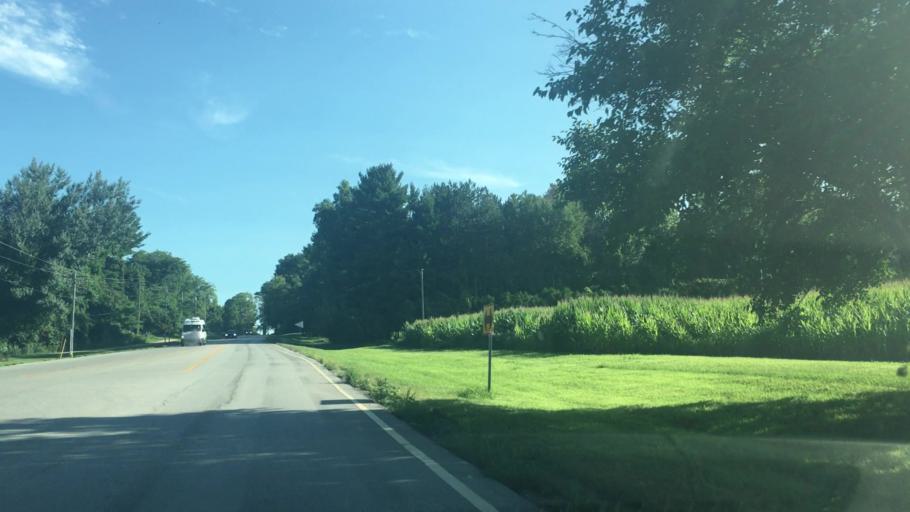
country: US
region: Iowa
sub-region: Johnson County
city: Iowa City
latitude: 41.6989
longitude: -91.5460
